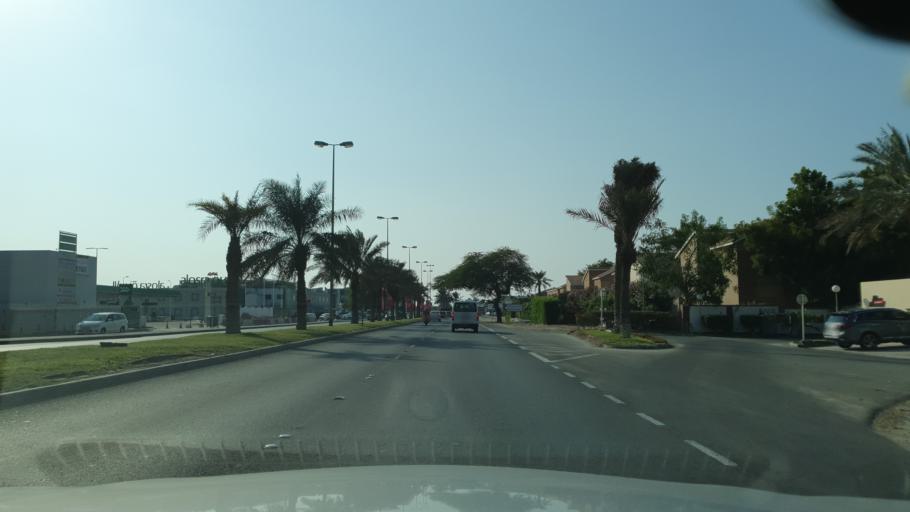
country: BH
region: Manama
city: Jidd Hafs
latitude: 26.2180
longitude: 50.4816
